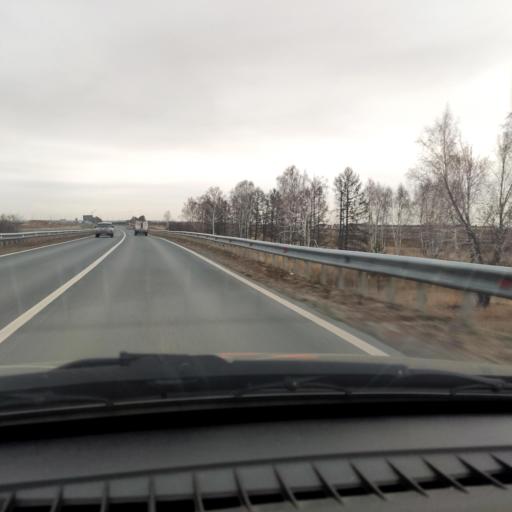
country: RU
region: Samara
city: Bereza
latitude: 53.4901
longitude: 50.1175
